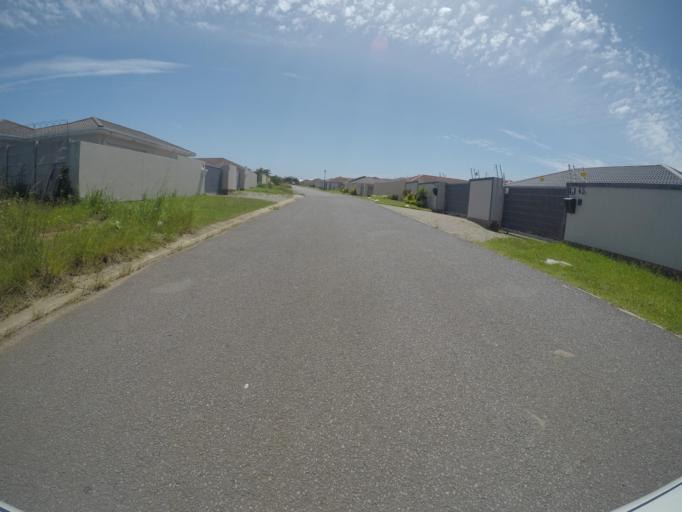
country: ZA
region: Eastern Cape
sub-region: Buffalo City Metropolitan Municipality
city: East London
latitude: -32.9437
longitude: 27.9960
